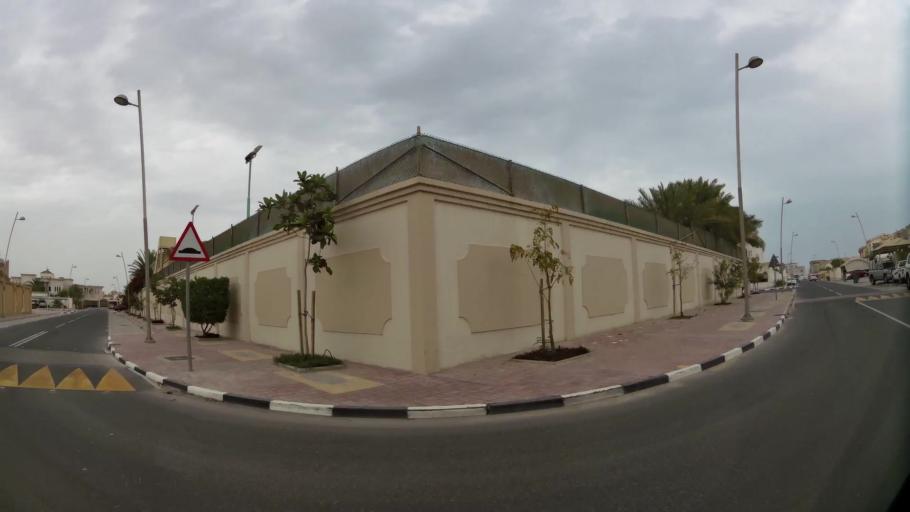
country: QA
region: Baladiyat ad Dawhah
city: Doha
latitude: 25.3387
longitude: 51.4835
